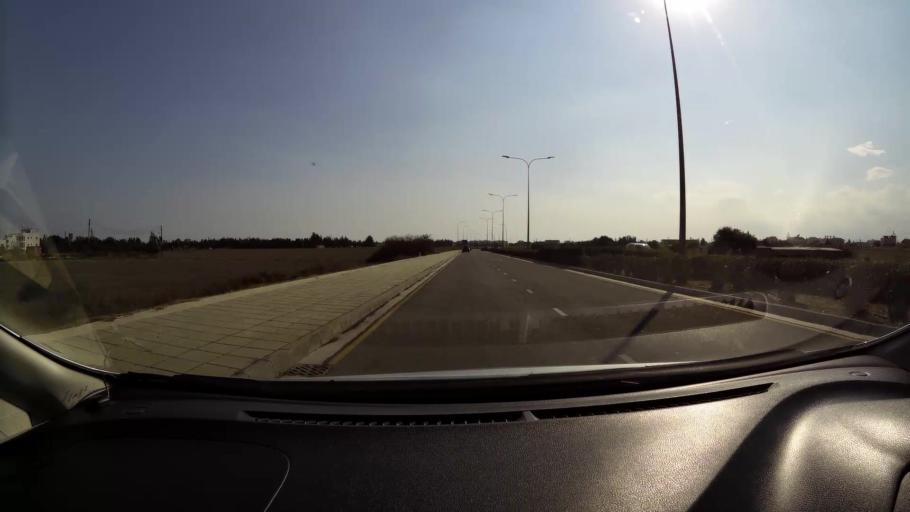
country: CY
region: Larnaka
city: Meneou
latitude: 34.8713
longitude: 33.5993
